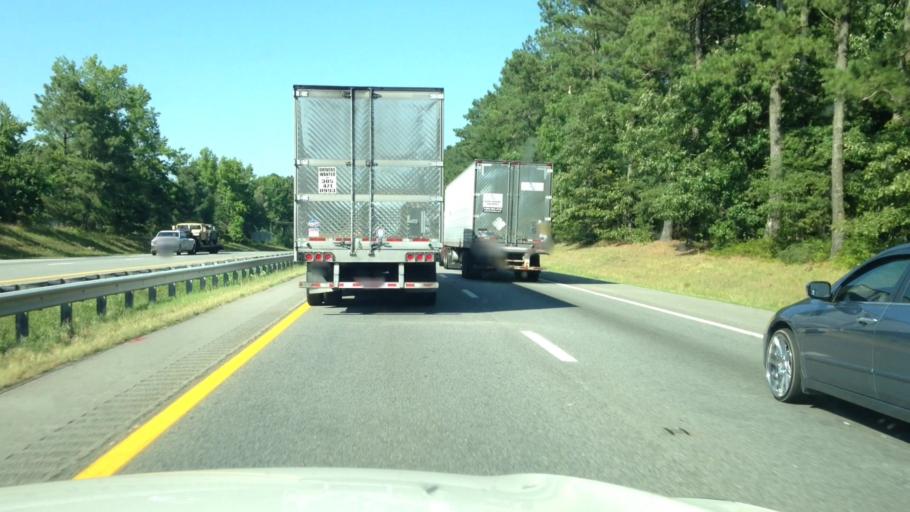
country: US
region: Virginia
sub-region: City of Emporia
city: Emporia
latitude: 36.7195
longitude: -77.5349
